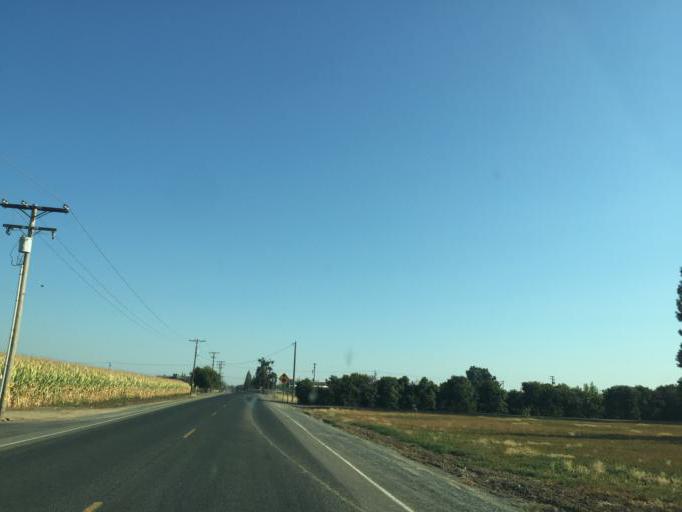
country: US
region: California
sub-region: Tulare County
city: Visalia
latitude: 36.3882
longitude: -119.2788
